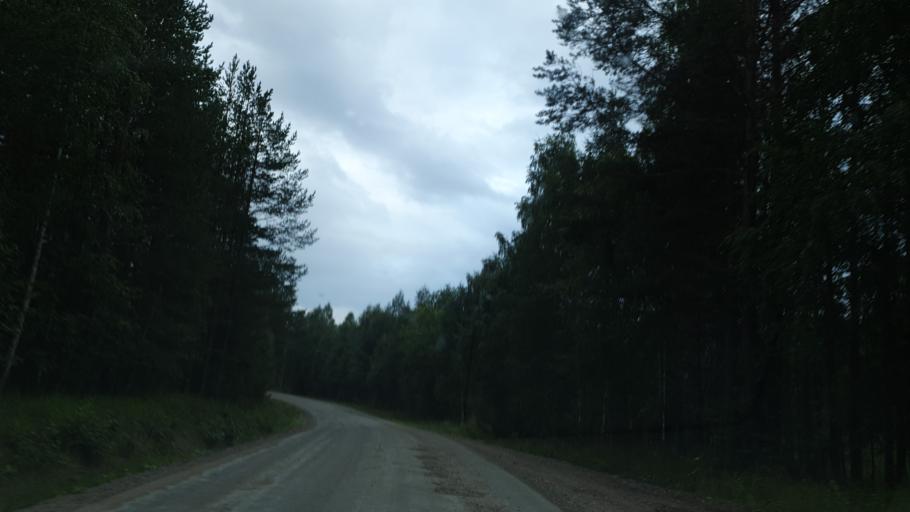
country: FI
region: Kainuu
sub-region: Kehys-Kainuu
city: Kuhmo
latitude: 64.1969
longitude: 29.3664
